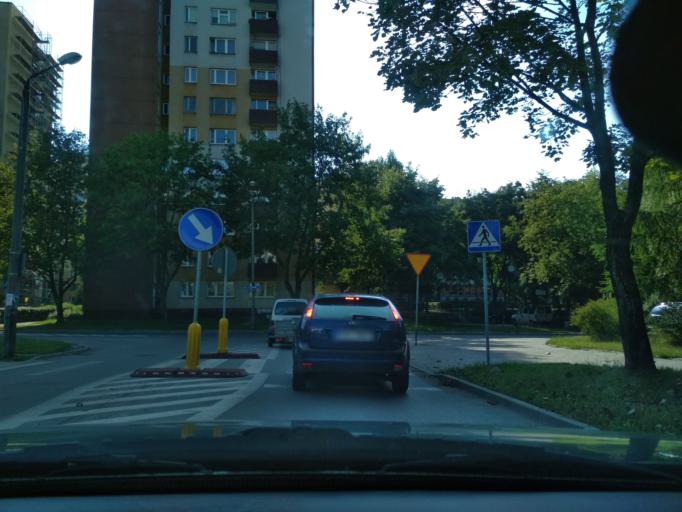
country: PL
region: Silesian Voivodeship
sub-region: Gliwice
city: Gliwice
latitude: 50.2767
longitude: 18.6583
